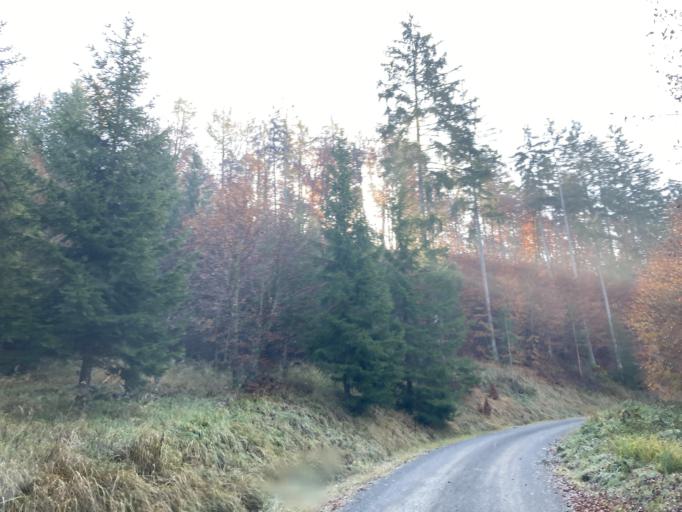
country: DE
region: Baden-Wuerttemberg
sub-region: Regierungsbezirk Stuttgart
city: Hildrizhausen
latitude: 48.5822
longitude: 8.9820
